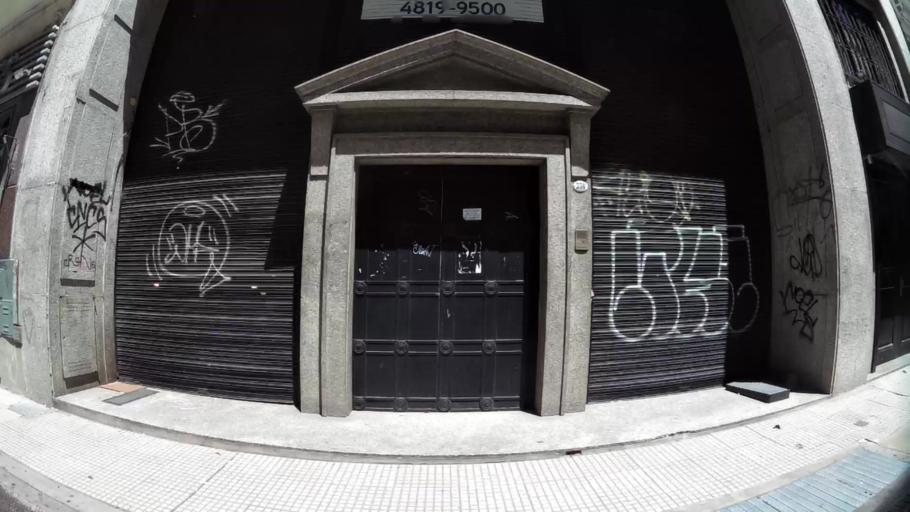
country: AR
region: Buenos Aires F.D.
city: Buenos Aires
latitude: -34.6056
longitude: -58.3718
